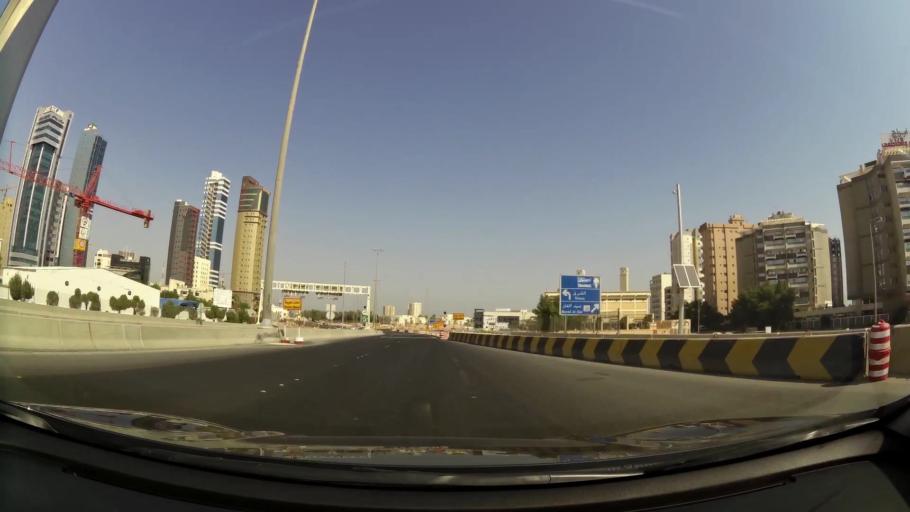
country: KW
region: Al Asimah
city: Ad Dasmah
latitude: 29.3772
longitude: 47.9974
